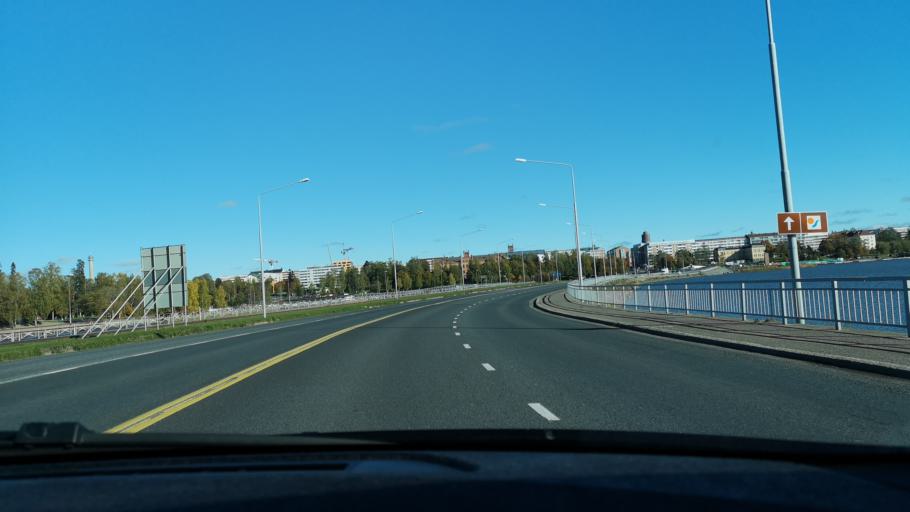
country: FI
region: Ostrobothnia
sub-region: Vaasa
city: Vaasa
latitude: 63.0920
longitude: 21.5915
